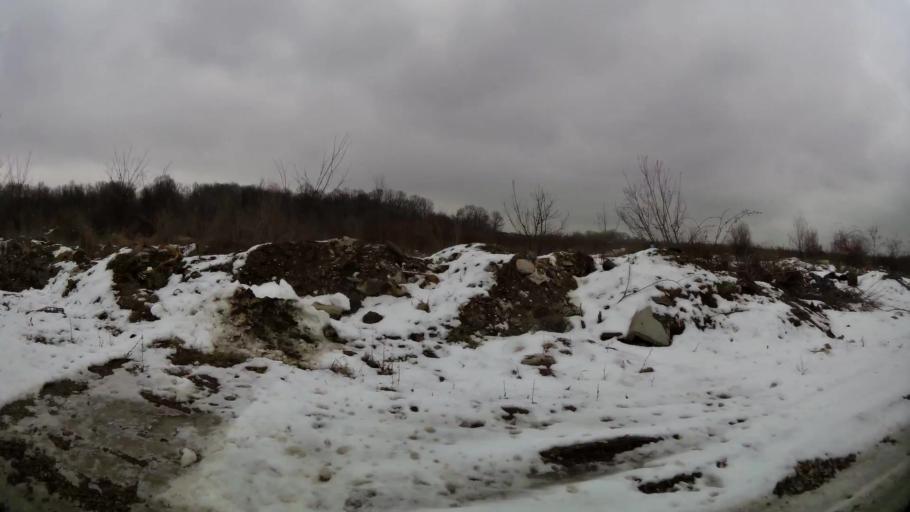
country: RO
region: Ilfov
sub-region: Comuna Mogosoaia
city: Mogosoaia
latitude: 44.5075
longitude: 26.0084
